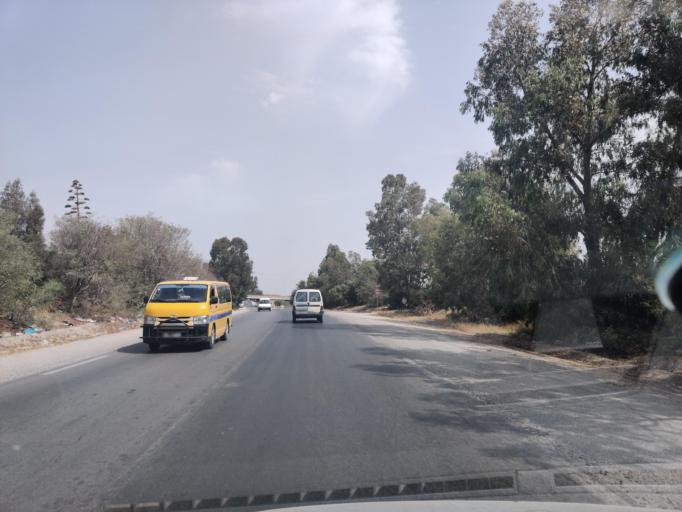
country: TN
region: Nabul
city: Al Hammamat
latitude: 36.4380
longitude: 10.5733
